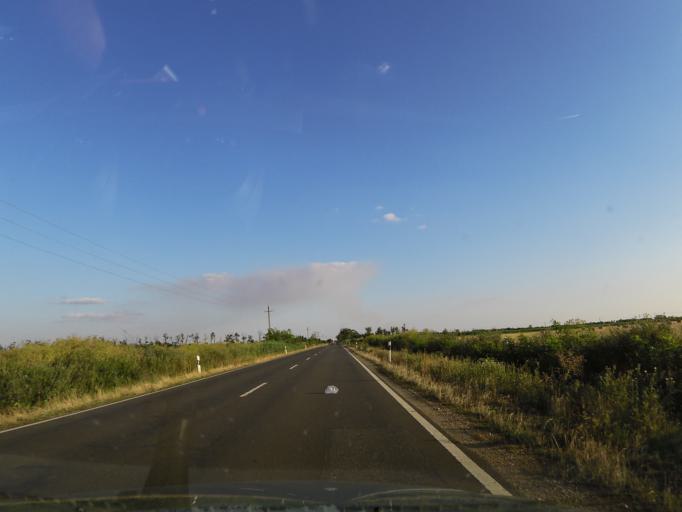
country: HU
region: Jasz-Nagykun-Szolnok
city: Kunszentmarton
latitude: 46.8724
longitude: 20.2654
